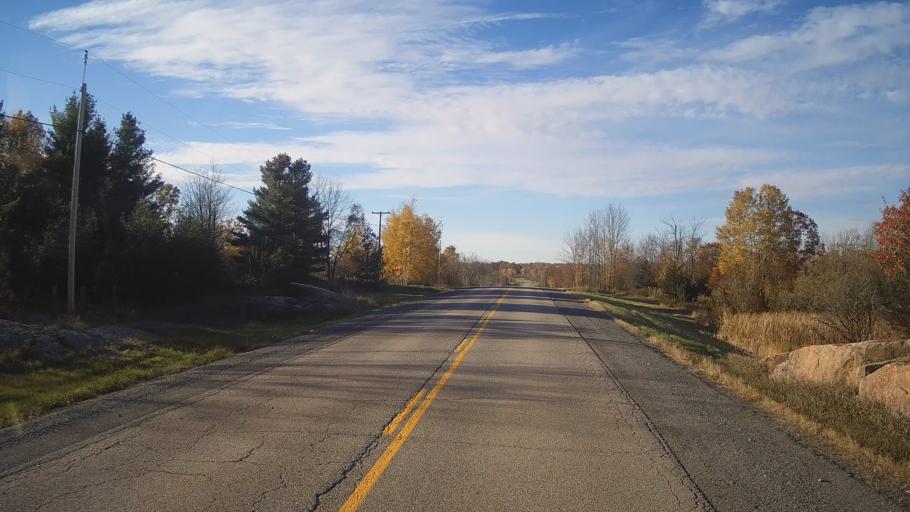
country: CA
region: Ontario
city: Perth
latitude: 44.7126
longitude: -76.4382
